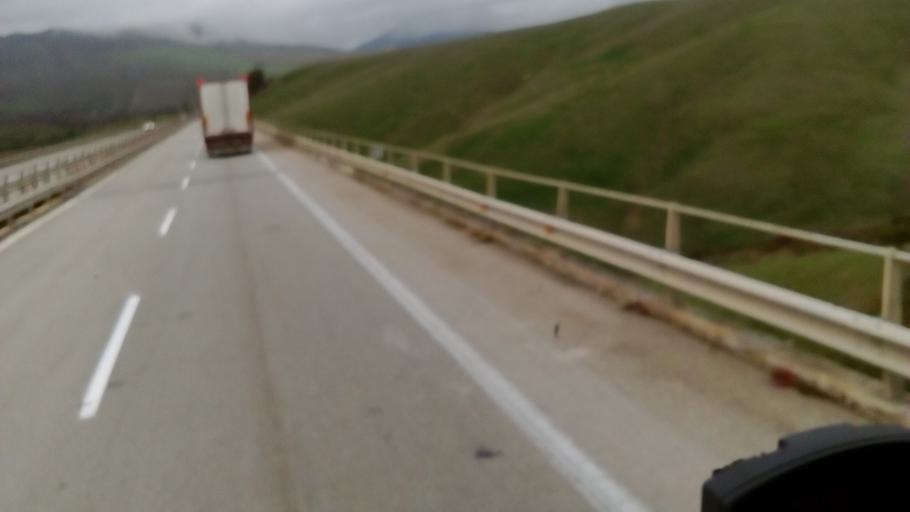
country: IT
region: Sicily
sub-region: Enna
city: Calascibetta
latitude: 37.5755
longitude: 14.2361
